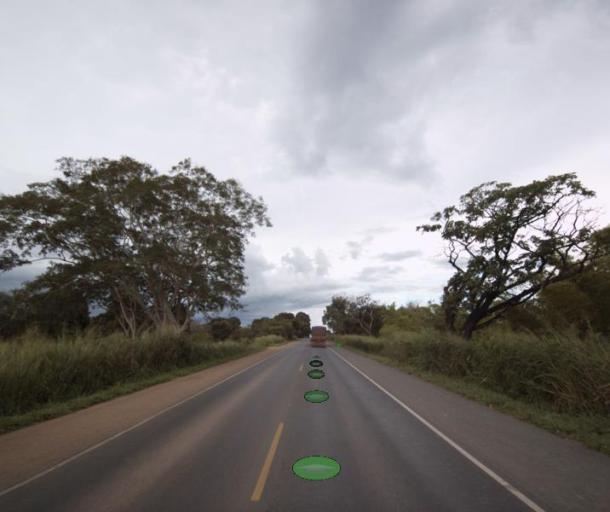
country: BR
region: Goias
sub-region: Itapaci
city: Itapaci
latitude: -15.0440
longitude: -49.4413
